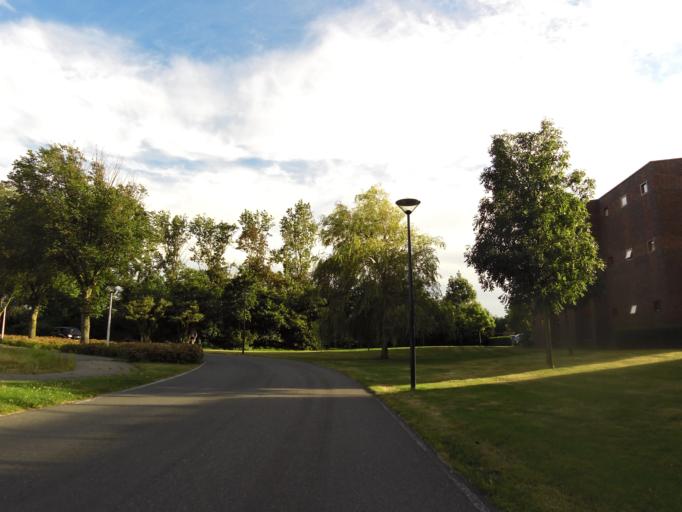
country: NL
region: South Holland
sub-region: Gemeente Noordwijk
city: Noordwijk-Binnen
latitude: 52.2201
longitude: 4.4263
